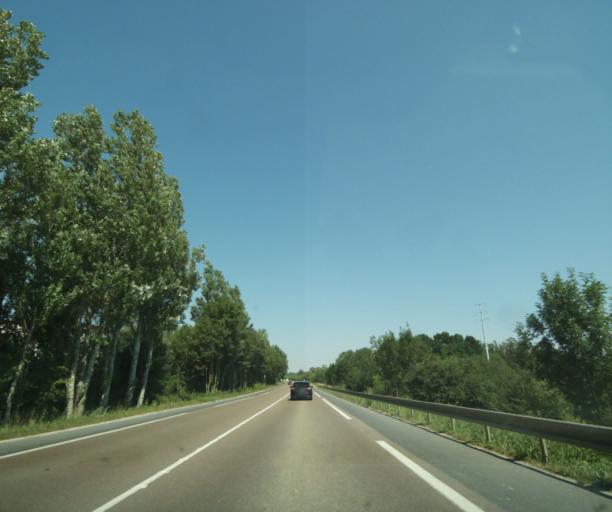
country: FR
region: Champagne-Ardenne
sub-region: Departement de la Marne
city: Frignicourt
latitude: 48.7256
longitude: 4.6255
